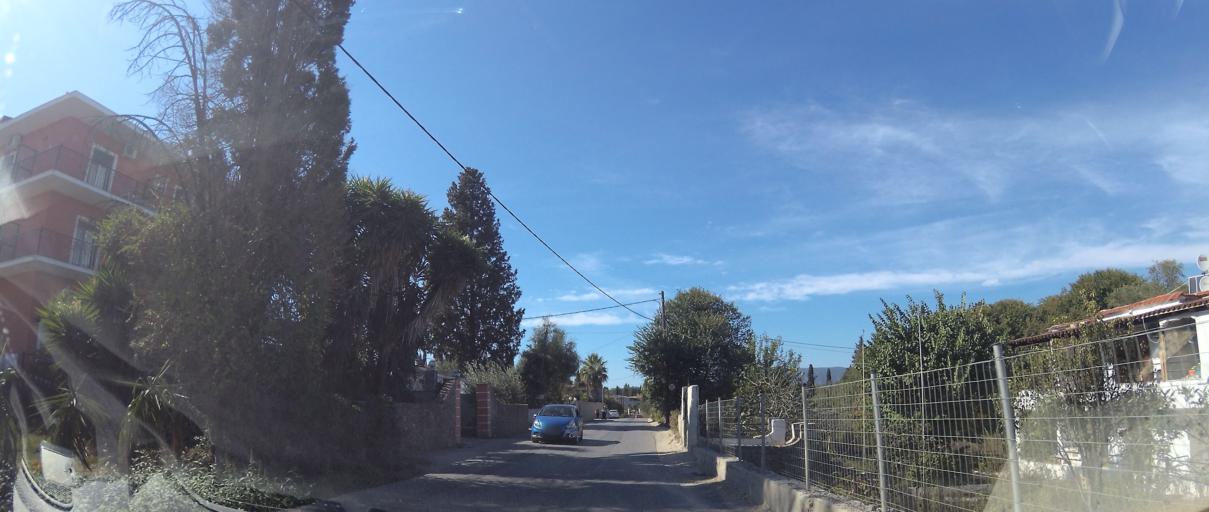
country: GR
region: Ionian Islands
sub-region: Nomos Kerkyras
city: Kontokali
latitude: 39.6436
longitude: 19.8489
